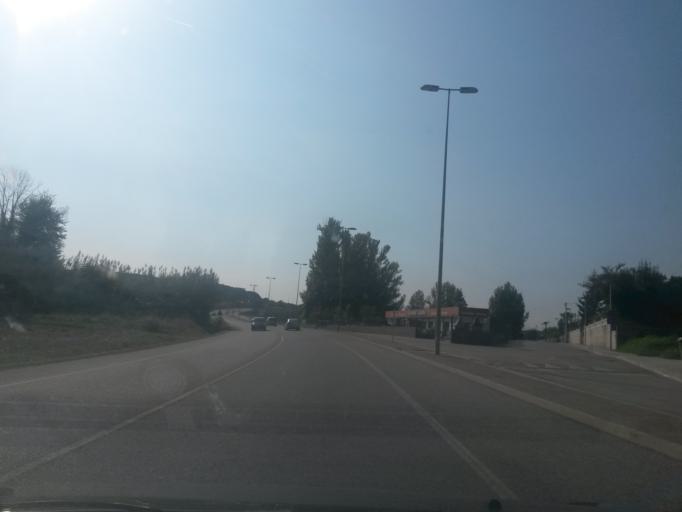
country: ES
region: Catalonia
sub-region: Provincia de Girona
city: Fornells de la Selva
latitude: 41.9467
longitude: 2.8053
